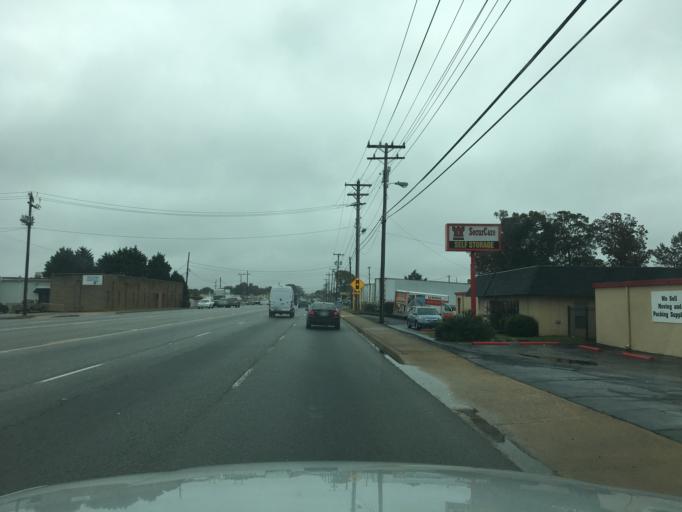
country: US
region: South Carolina
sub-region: Greenville County
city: Gantt
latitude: 34.8082
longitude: -82.4355
